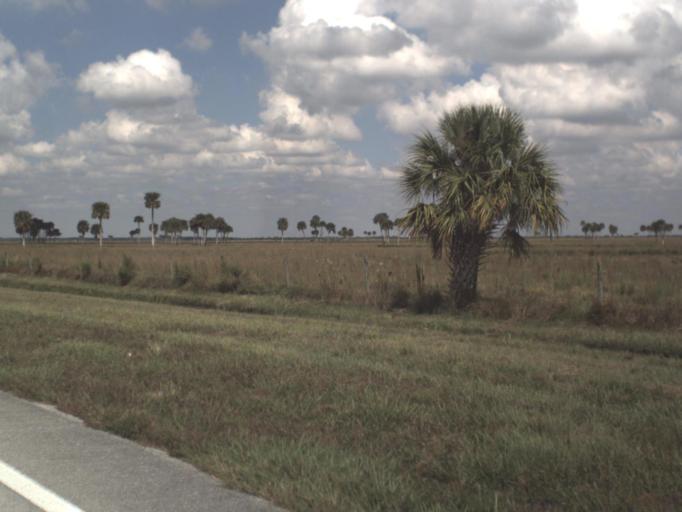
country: US
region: Florida
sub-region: Okeechobee County
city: Okeechobee
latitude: 27.3403
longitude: -80.9402
